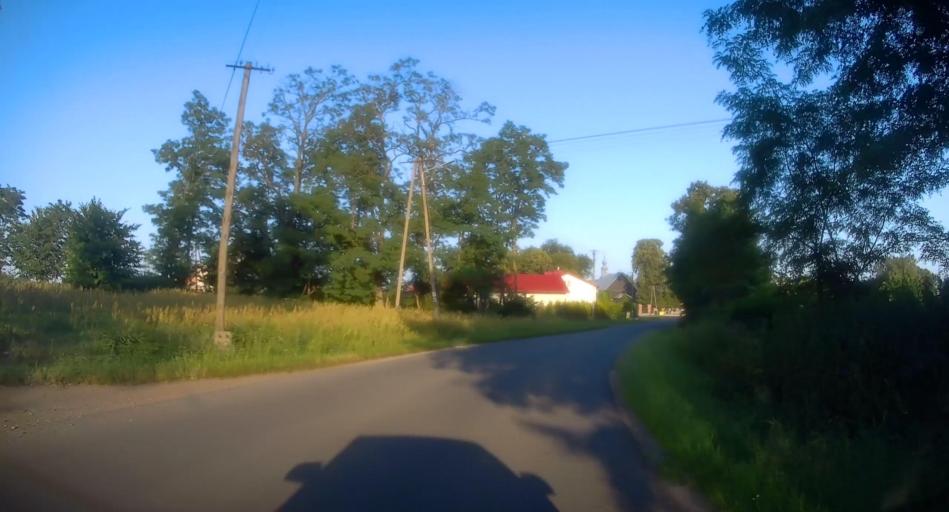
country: PL
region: Lodz Voivodeship
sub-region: Powiat skierniewicki
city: Kaweczyn Nowy
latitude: 51.8835
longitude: 20.2711
